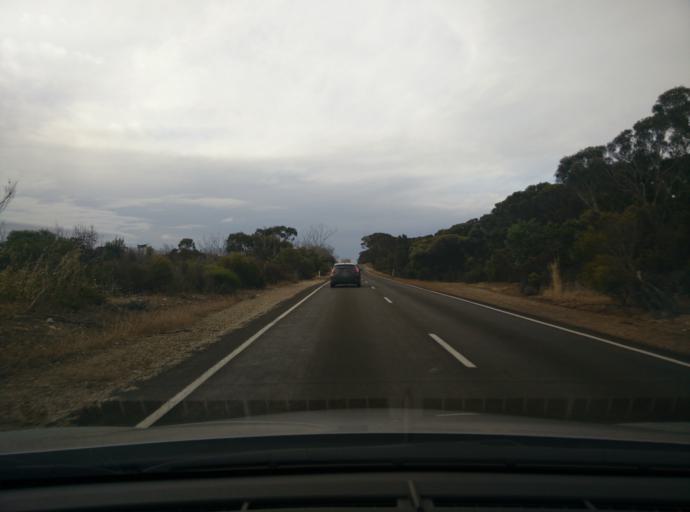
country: AU
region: South Australia
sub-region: Kangaroo Island
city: Kingscote
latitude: -35.7667
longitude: 137.6178
